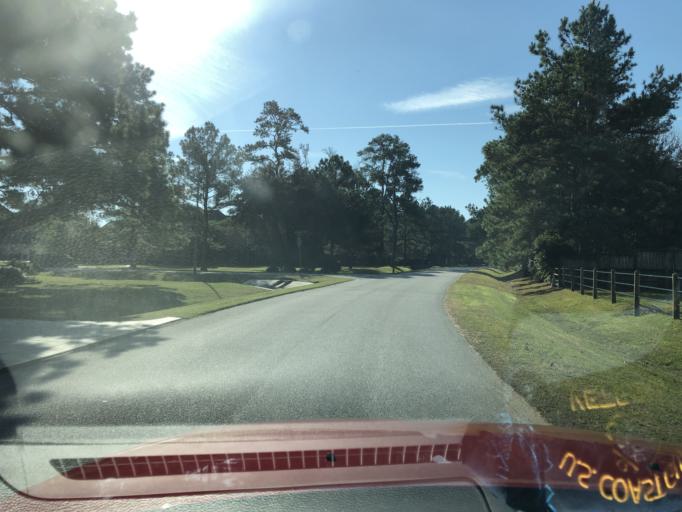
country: US
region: Texas
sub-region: Harris County
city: Tomball
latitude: 30.0416
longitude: -95.5604
